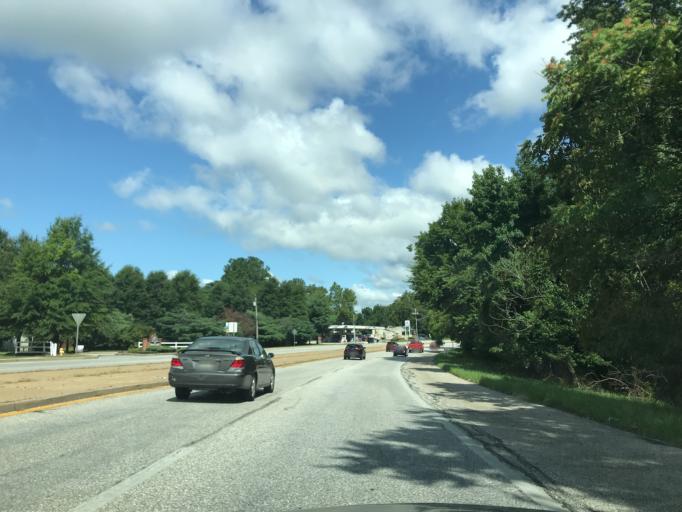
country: US
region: Maryland
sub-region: Anne Arundel County
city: Green Haven
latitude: 39.1826
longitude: -76.5501
